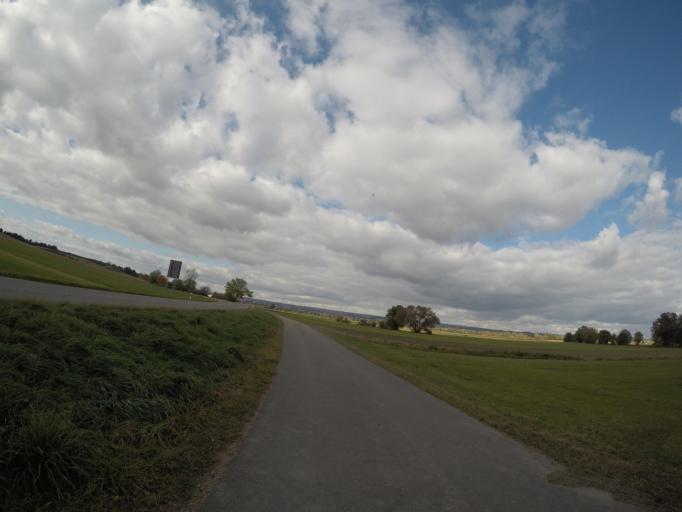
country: DE
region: Baden-Wuerttemberg
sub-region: Tuebingen Region
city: Unterstadion
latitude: 48.2069
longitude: 9.6799
